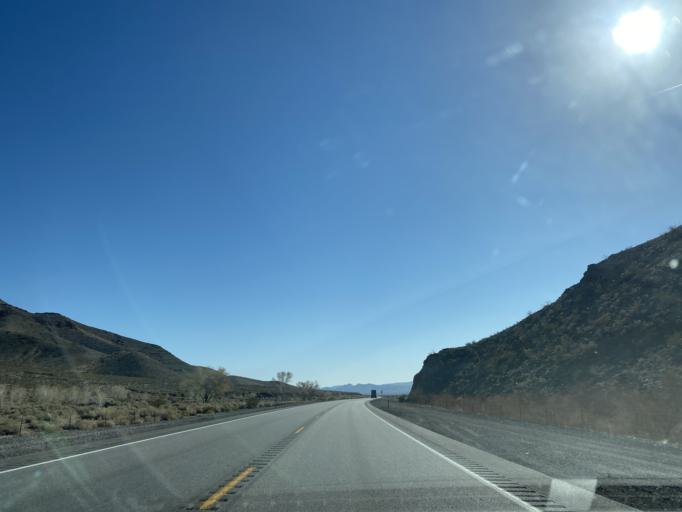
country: US
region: Nevada
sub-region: Nye County
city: Beatty
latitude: 36.8868
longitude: -116.7513
